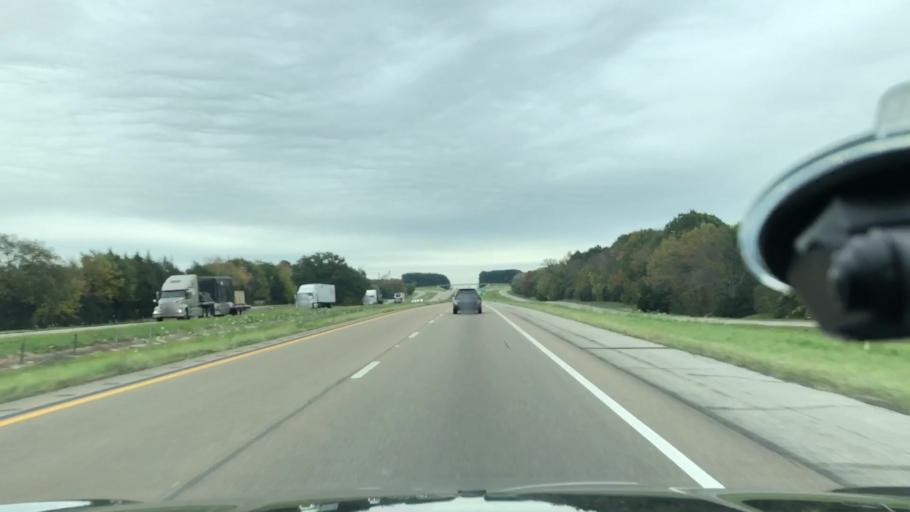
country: US
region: Texas
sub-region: Titus County
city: Mount Pleasant
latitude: 33.1596
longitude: -95.0864
